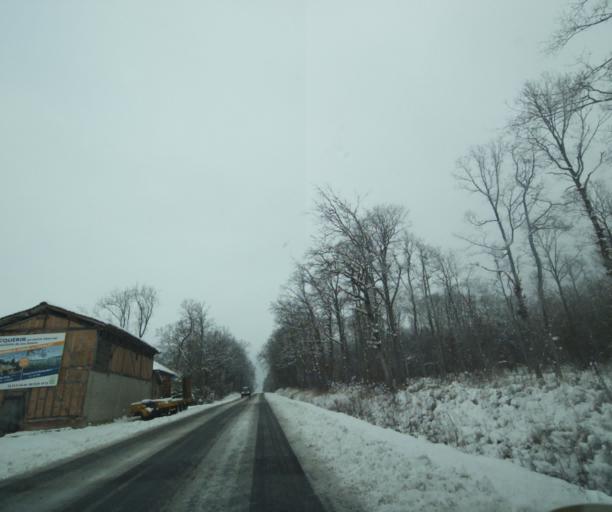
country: FR
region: Champagne-Ardenne
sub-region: Departement de la Haute-Marne
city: Montier-en-Der
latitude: 48.5255
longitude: 4.7485
